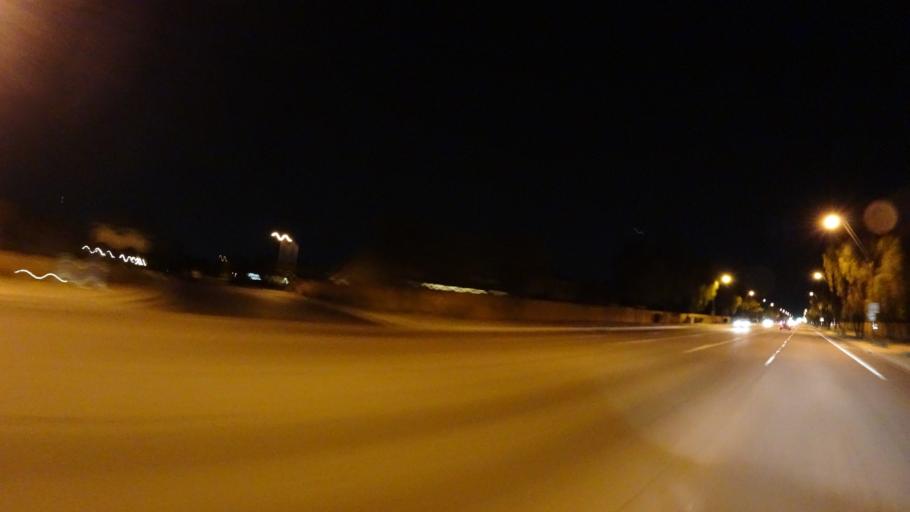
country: US
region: Arizona
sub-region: Maricopa County
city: San Carlos
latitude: 33.3347
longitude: -111.9065
